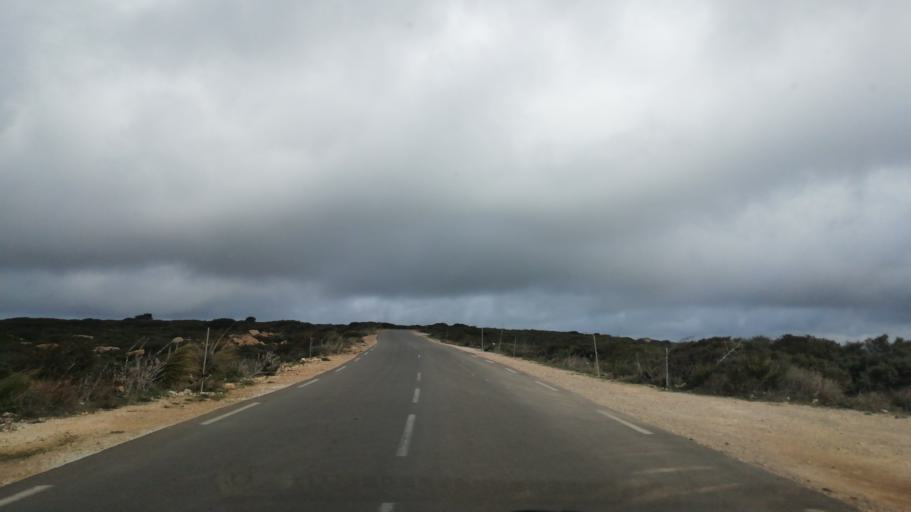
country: DZ
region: Oran
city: Mers el Kebir
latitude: 35.7031
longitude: -0.7394
